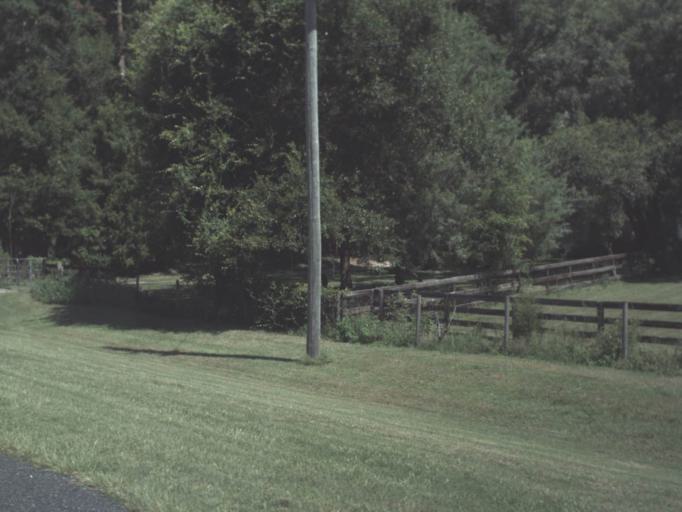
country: US
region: Florida
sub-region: Levy County
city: Williston
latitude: 29.3922
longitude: -82.4768
